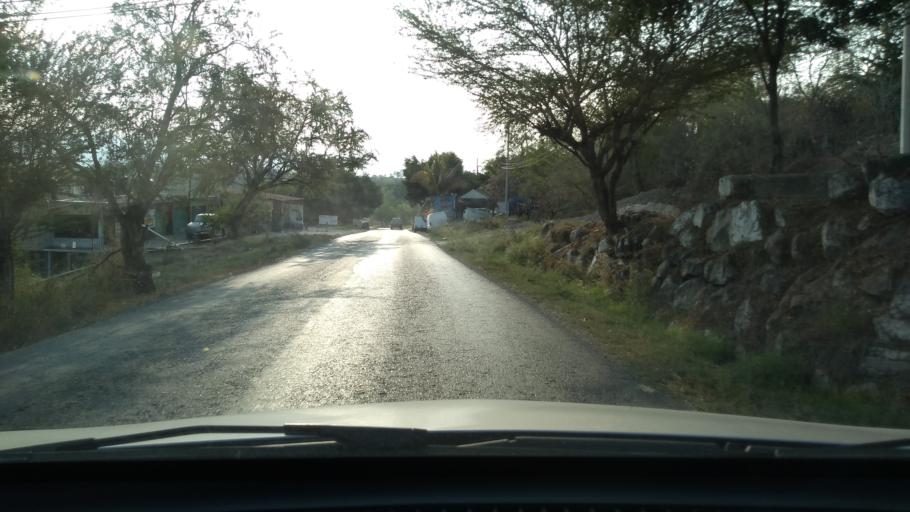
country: MX
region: Morelos
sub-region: Jojutla
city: Tehuixtla
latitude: 18.5720
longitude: -99.2658
